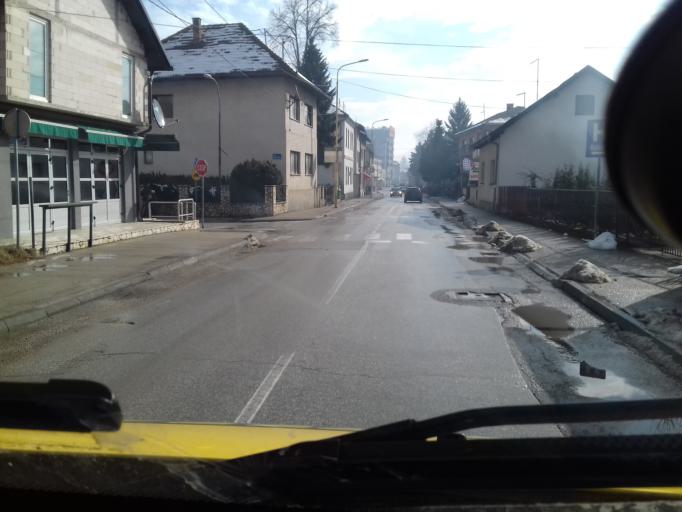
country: BA
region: Federation of Bosnia and Herzegovina
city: Zepce
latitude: 44.4242
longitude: 18.0316
